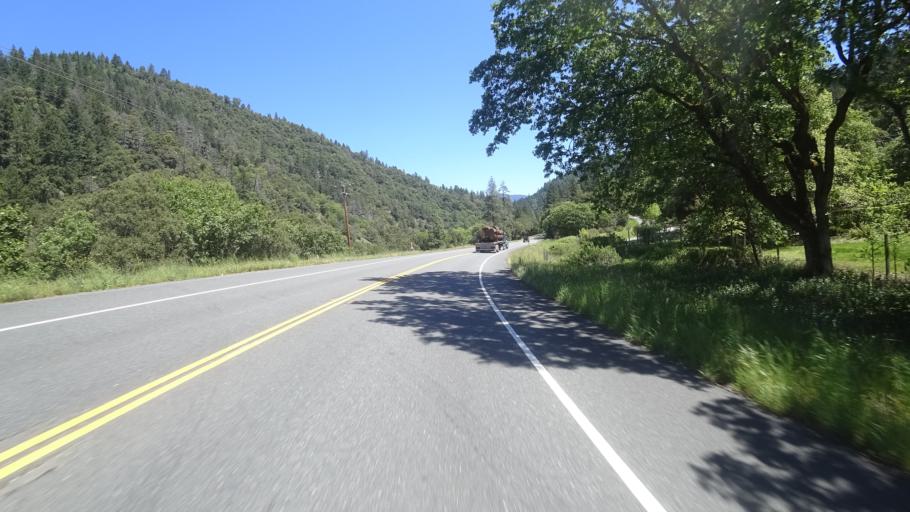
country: US
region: California
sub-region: Humboldt County
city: Willow Creek
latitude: 40.8891
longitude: -123.6007
